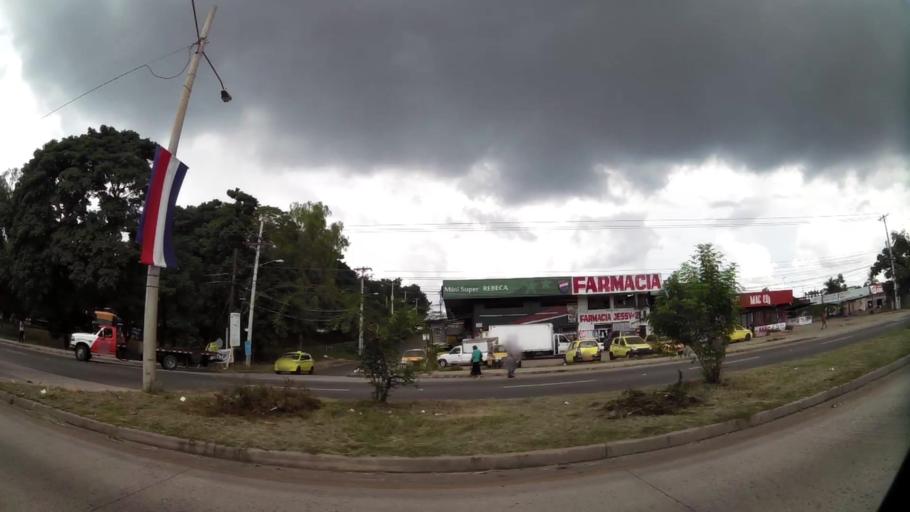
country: PA
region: Panama
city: Cabra Numero Uno
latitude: 9.1005
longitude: -79.3302
